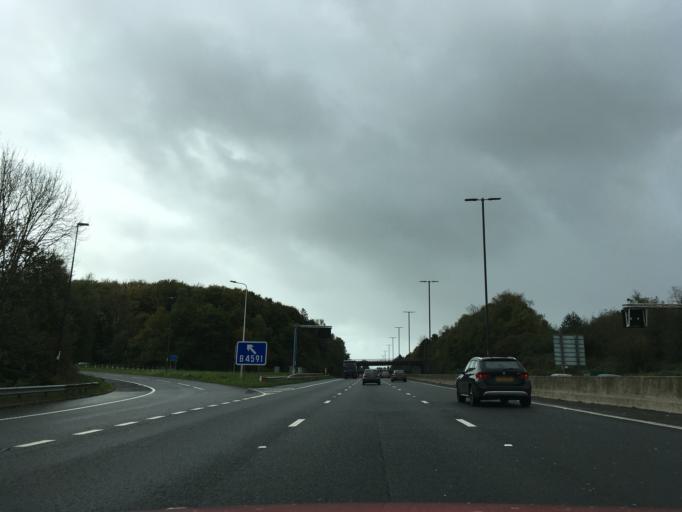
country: GB
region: Wales
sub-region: Newport
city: Newport
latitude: 51.5877
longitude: -3.0327
